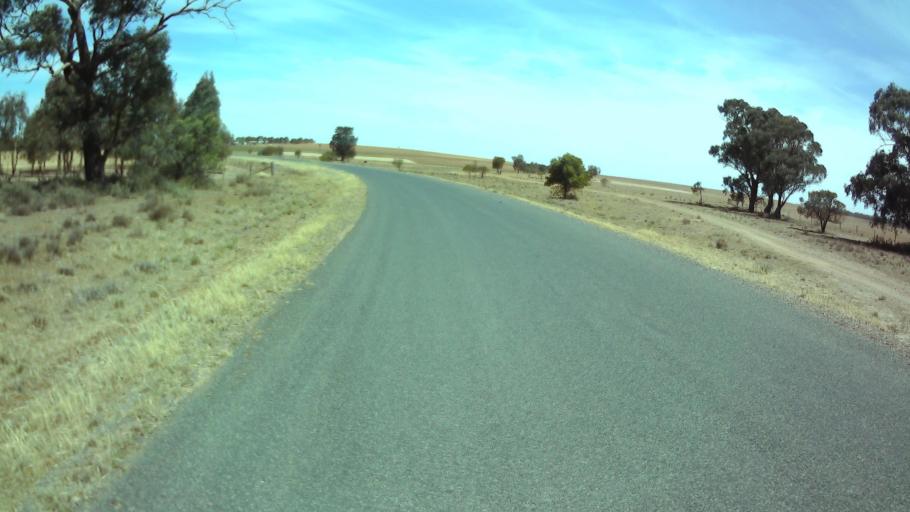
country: AU
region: New South Wales
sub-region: Weddin
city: Grenfell
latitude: -33.8877
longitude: 147.7417
